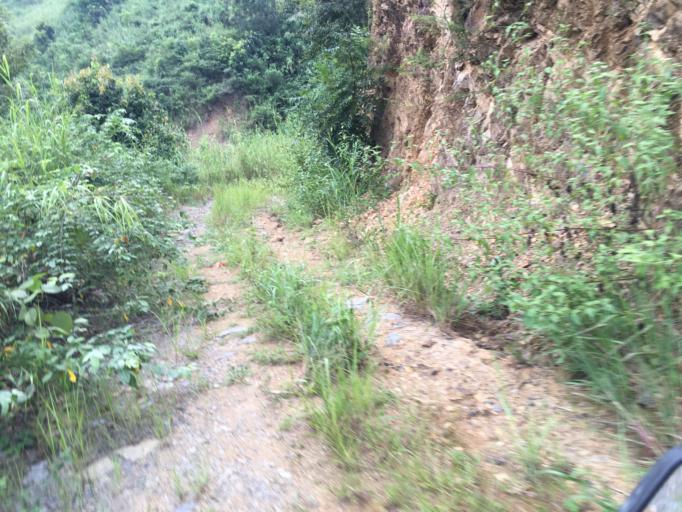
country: CN
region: Guangxi Zhuangzu Zizhiqu
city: Xinzhou
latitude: 25.1887
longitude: 105.8894
